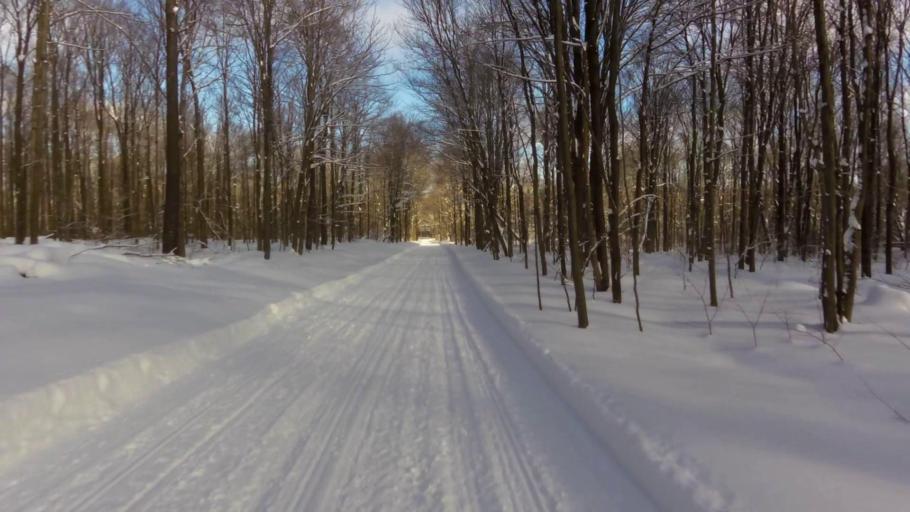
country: US
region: New York
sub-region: Chautauqua County
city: Falconer
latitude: 42.2682
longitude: -79.1417
